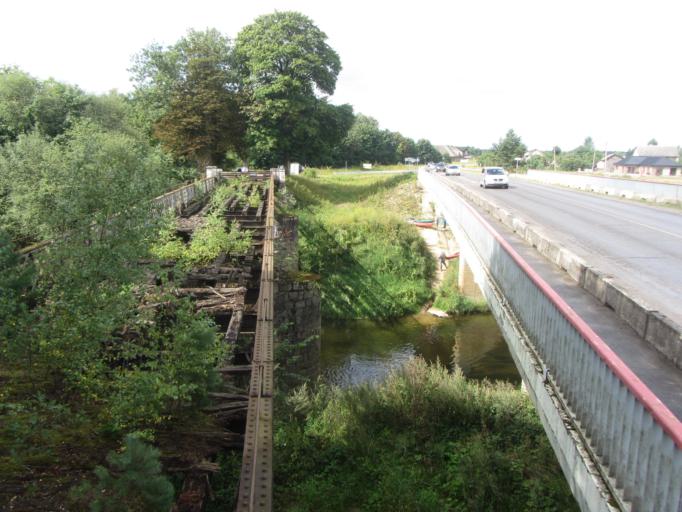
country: LT
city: Priekule
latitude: 55.6388
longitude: 21.3078
